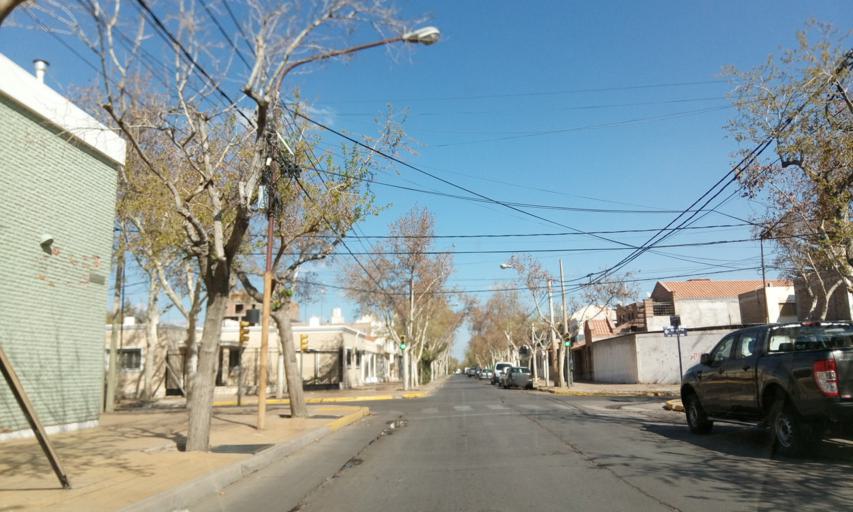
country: AR
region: San Juan
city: San Juan
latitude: -31.5415
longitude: -68.5281
